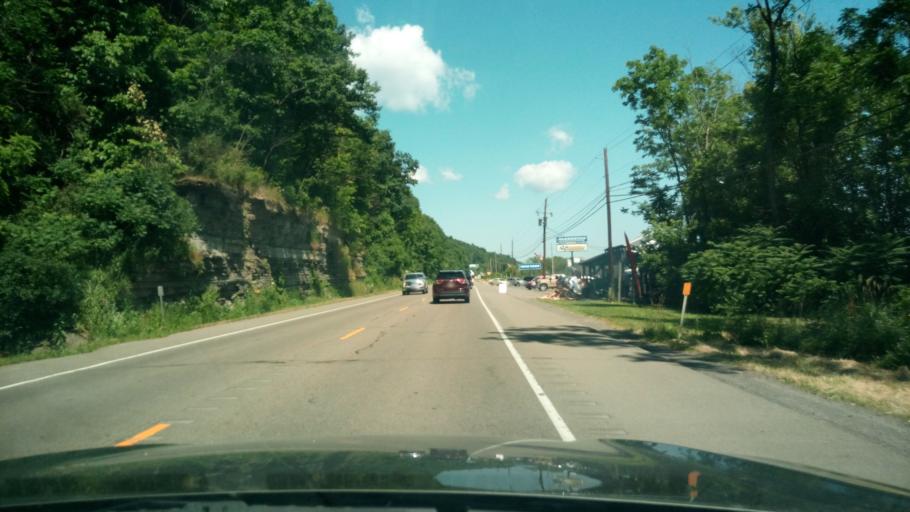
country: US
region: New York
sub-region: Schuyler County
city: Montour Falls
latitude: 42.3604
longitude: -76.8617
